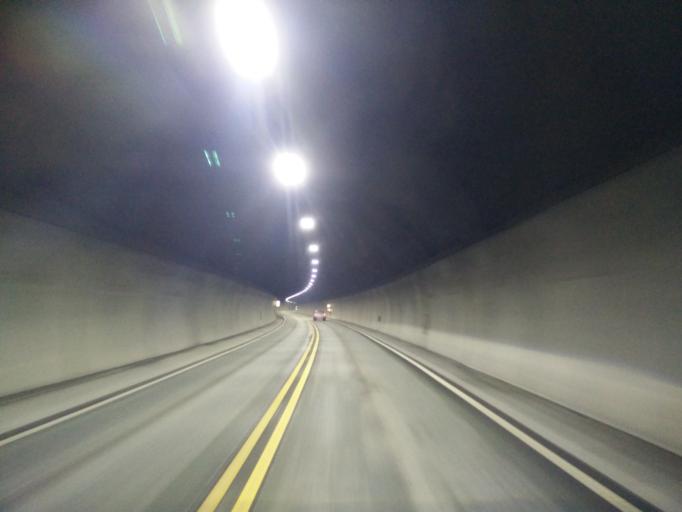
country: NO
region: Sor-Trondelag
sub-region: Melhus
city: Melhus
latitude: 63.3119
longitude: 10.1969
